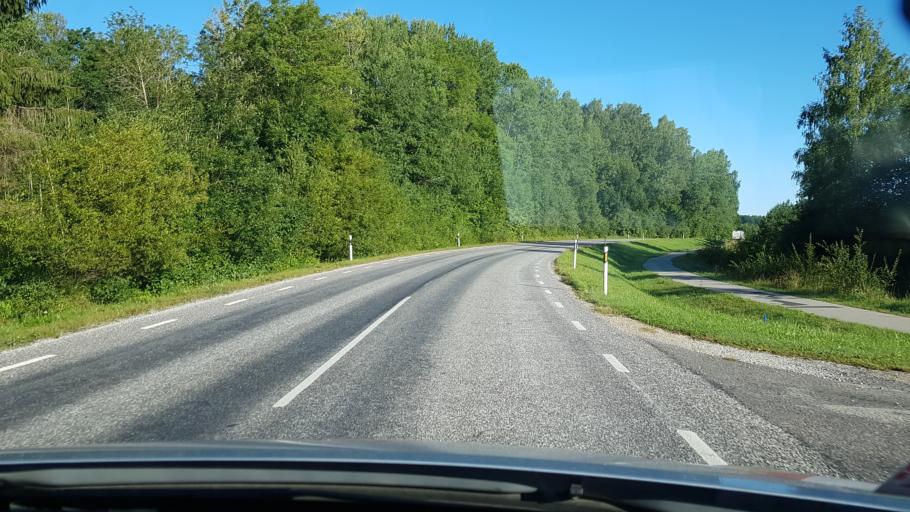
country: EE
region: Vorumaa
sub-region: Antsla vald
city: Vana-Antsla
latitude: 58.0450
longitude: 26.5471
